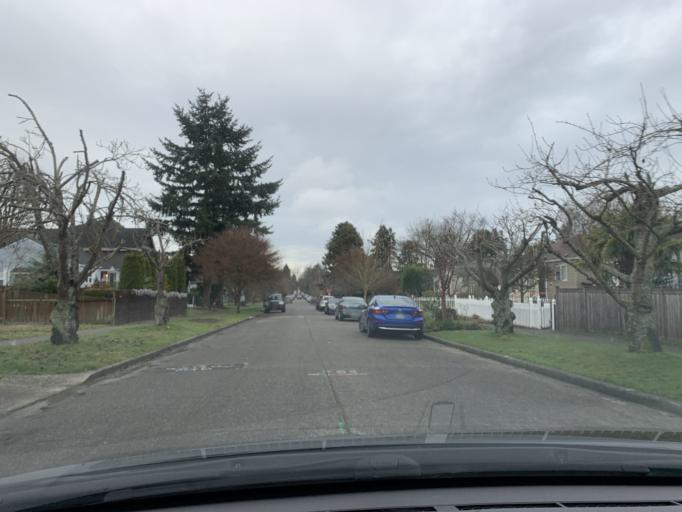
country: US
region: Washington
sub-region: King County
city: White Center
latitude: 47.5603
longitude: -122.3936
